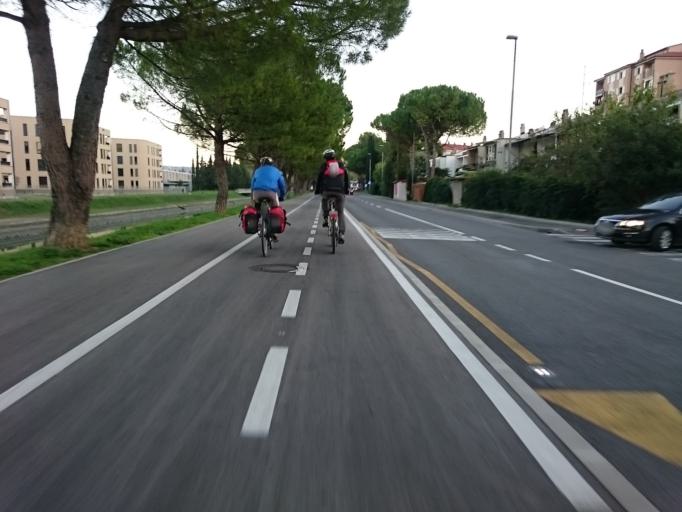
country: SI
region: Koper-Capodistria
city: Koper
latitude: 45.5372
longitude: 13.7277
